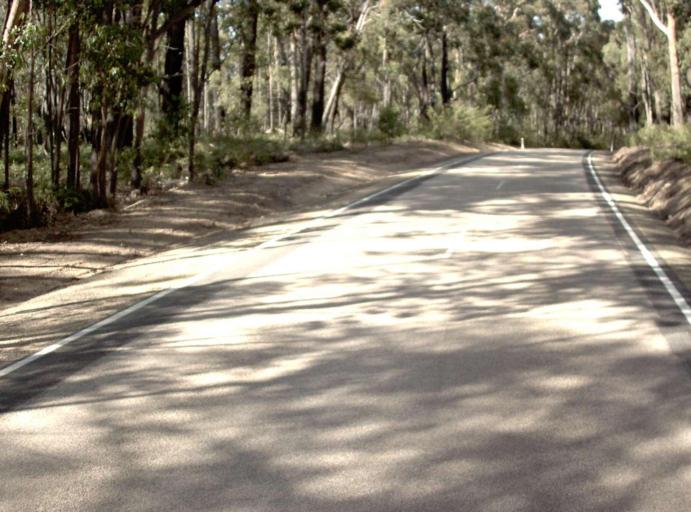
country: AU
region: Victoria
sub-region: East Gippsland
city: Lakes Entrance
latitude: -37.6872
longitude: 148.0483
